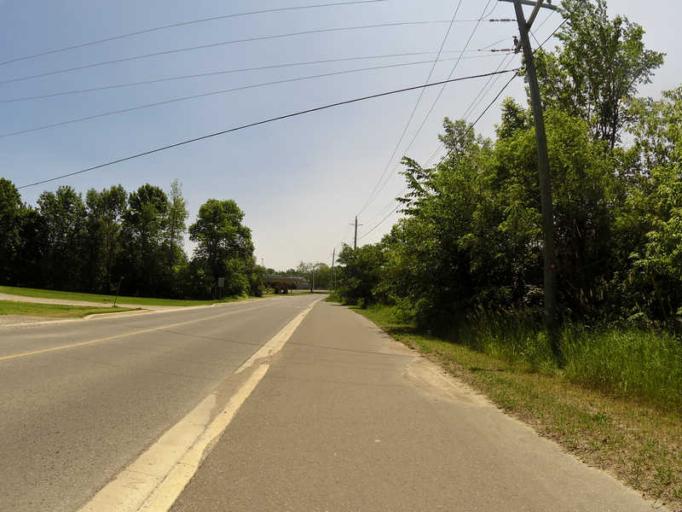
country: CA
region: Ontario
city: Peterborough
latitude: 44.4206
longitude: -78.2700
